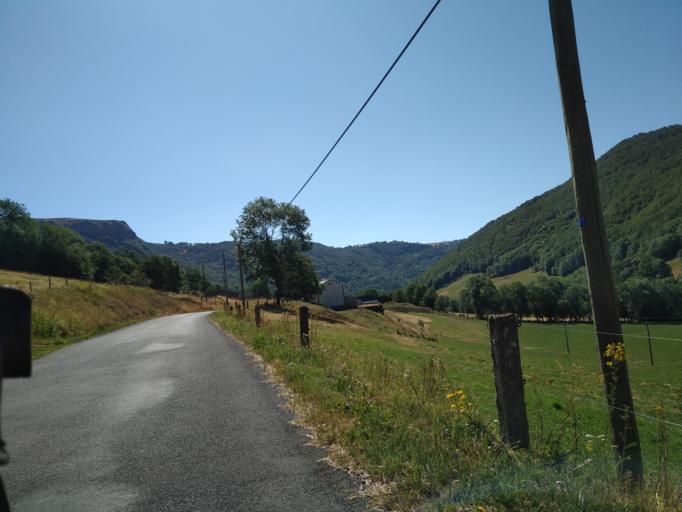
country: FR
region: Auvergne
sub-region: Departement du Cantal
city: Pierrefort
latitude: 45.0071
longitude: 2.7903
